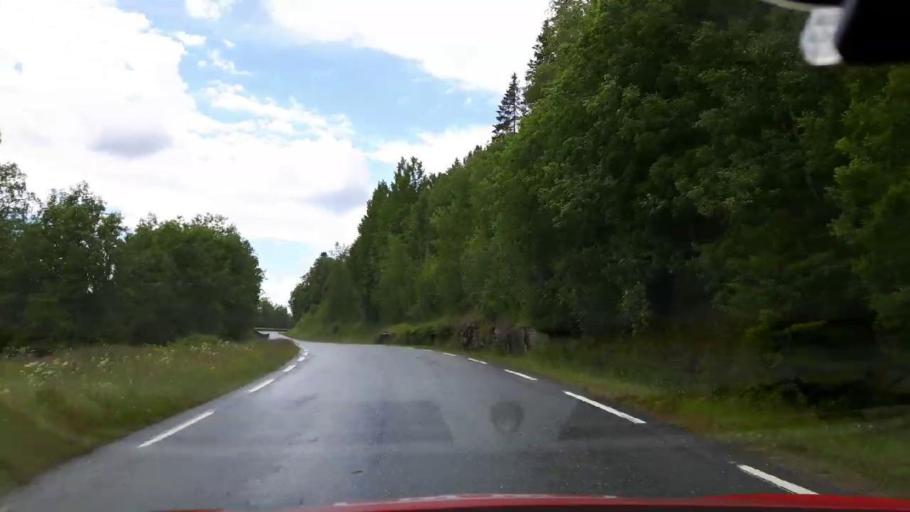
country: NO
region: Nord-Trondelag
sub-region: Lierne
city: Sandvika
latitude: 64.1057
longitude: 13.9909
